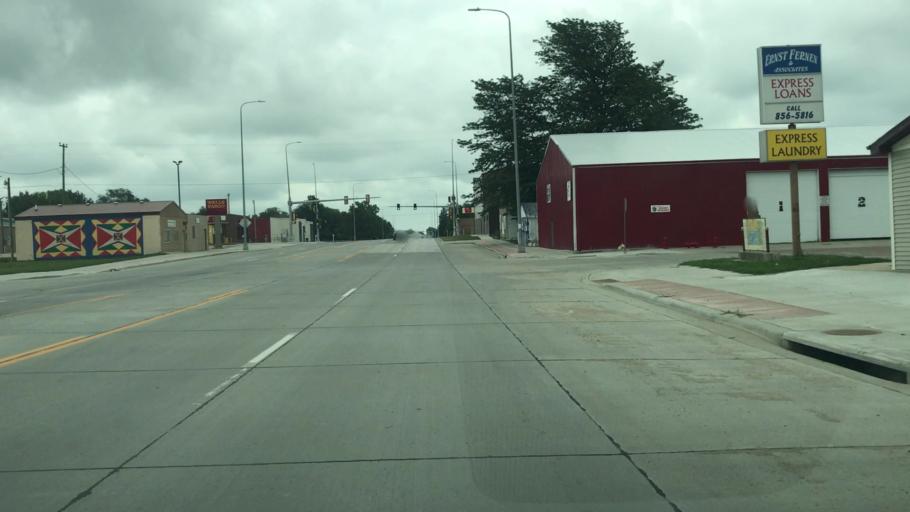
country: US
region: South Dakota
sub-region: Todd County
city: Mission
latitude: 43.3057
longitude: -100.6604
